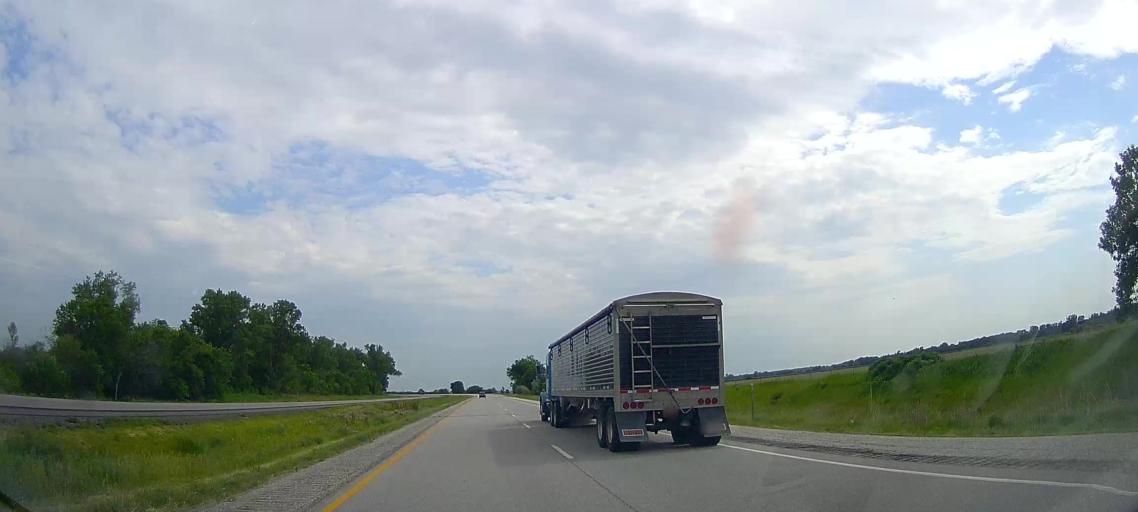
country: US
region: Nebraska
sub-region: Burt County
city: Tekamah
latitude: 41.7895
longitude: -96.0523
